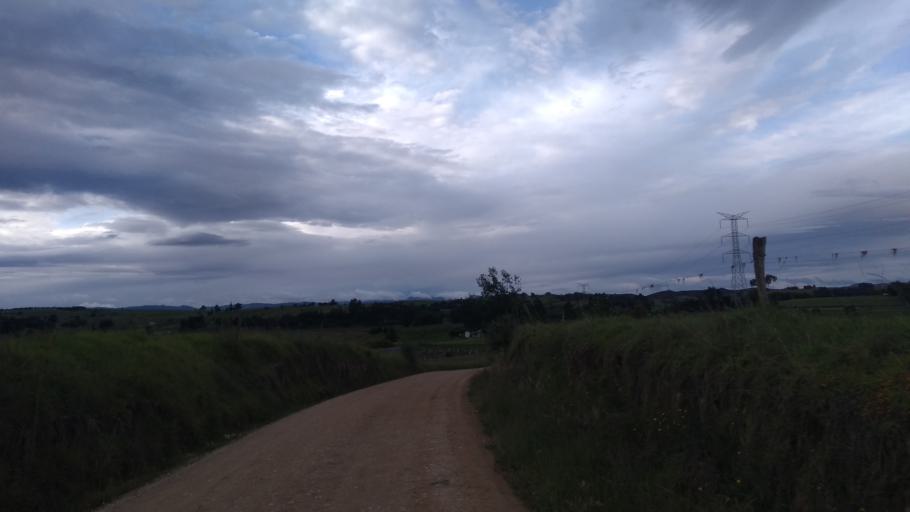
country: CO
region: Boyaca
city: Toca
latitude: 5.6123
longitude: -73.1745
